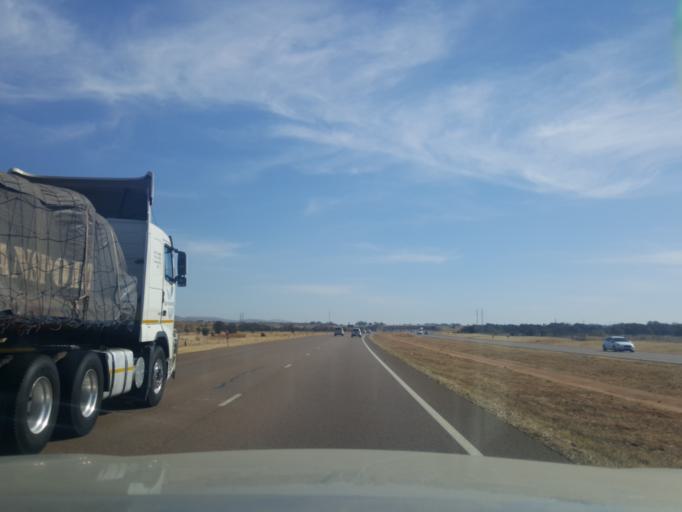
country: ZA
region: Gauteng
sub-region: City of Tshwane Metropolitan Municipality
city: Pretoria
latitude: -25.6460
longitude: 28.1635
